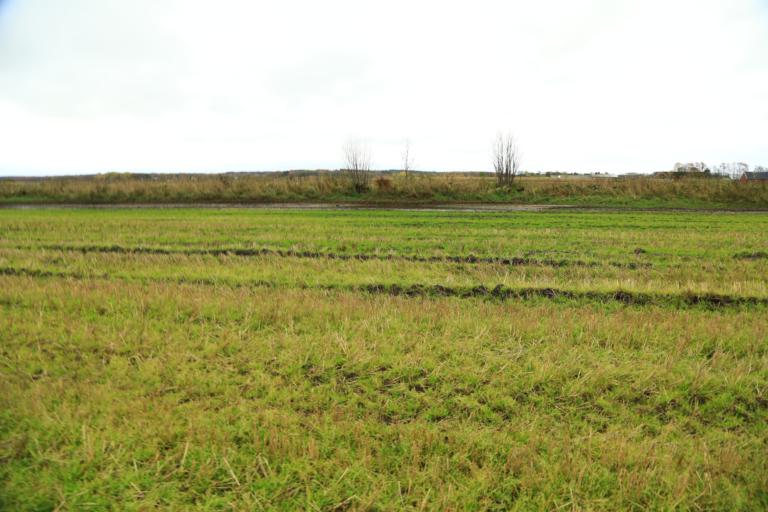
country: SE
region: Halland
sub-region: Varbergs Kommun
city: Traslovslage
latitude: 57.0972
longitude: 12.3028
